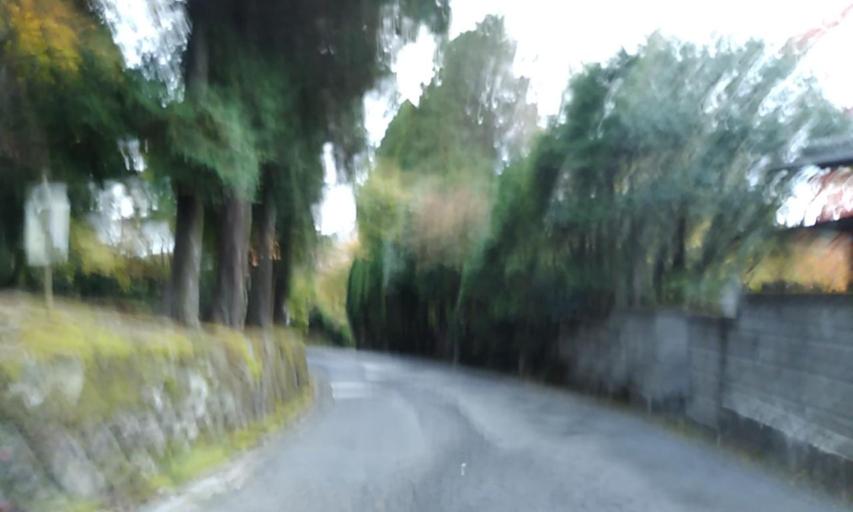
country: JP
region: Kanagawa
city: Hakone
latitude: 35.2486
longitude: 139.0009
